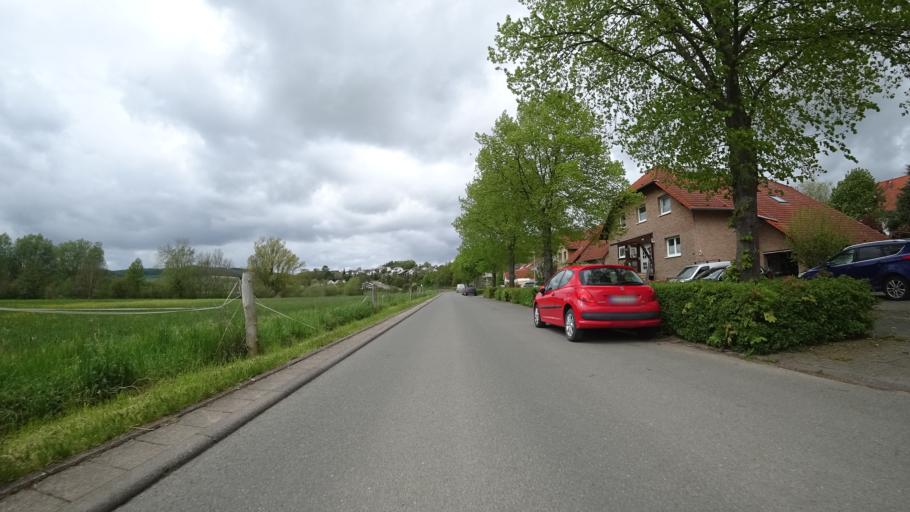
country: DE
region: Hesse
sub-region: Regierungsbezirk Kassel
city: Zierenberg
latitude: 51.4376
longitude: 9.3243
